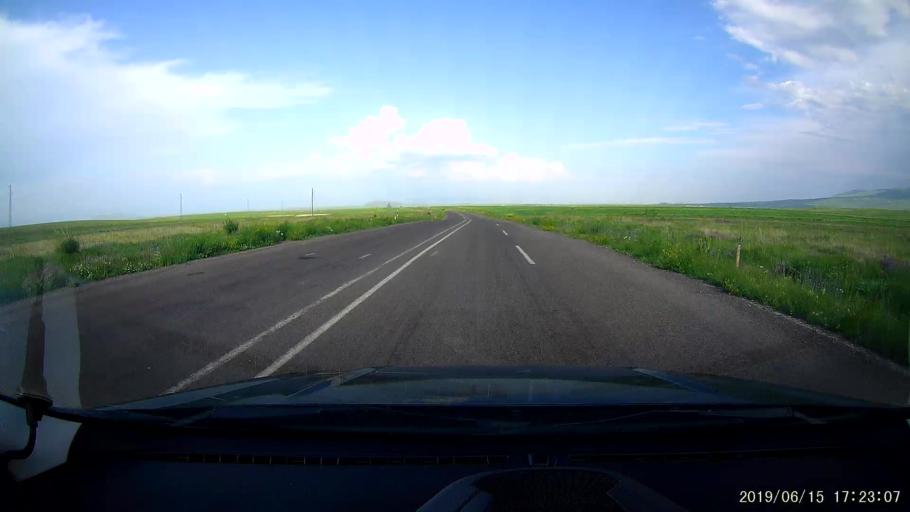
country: TR
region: Kars
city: Basgedikler
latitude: 40.6176
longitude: 43.3557
